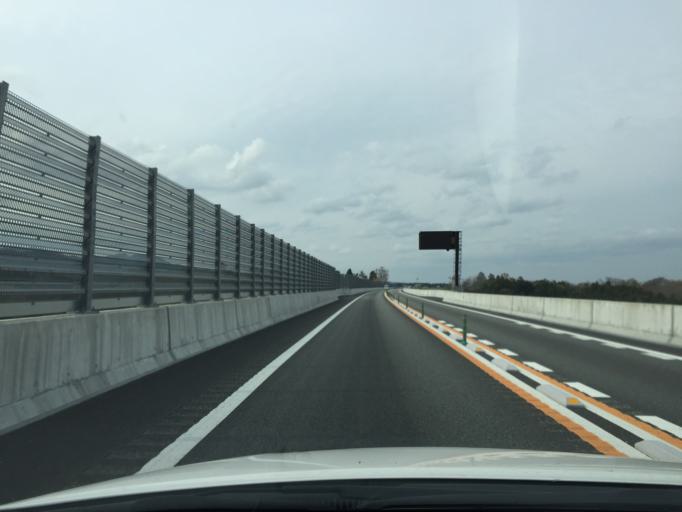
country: JP
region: Fukushima
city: Namie
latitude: 37.5968
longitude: 140.9263
